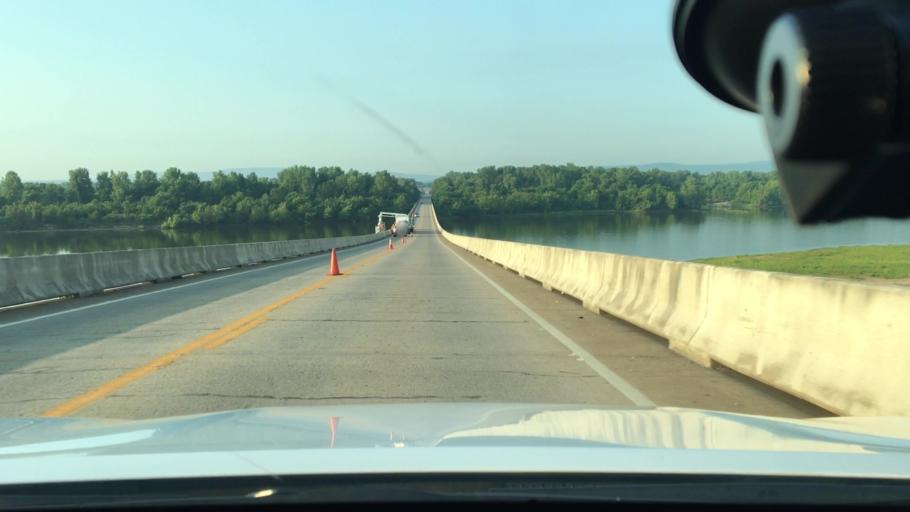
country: US
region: Arkansas
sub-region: Johnson County
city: Clarksville
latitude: 35.4094
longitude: -93.5319
